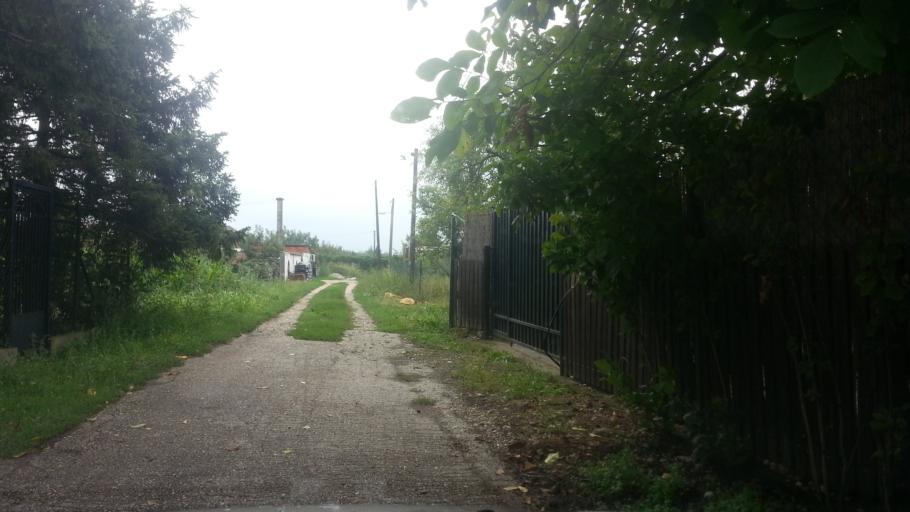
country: RS
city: Novi Banovci
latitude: 44.9407
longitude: 20.2958
